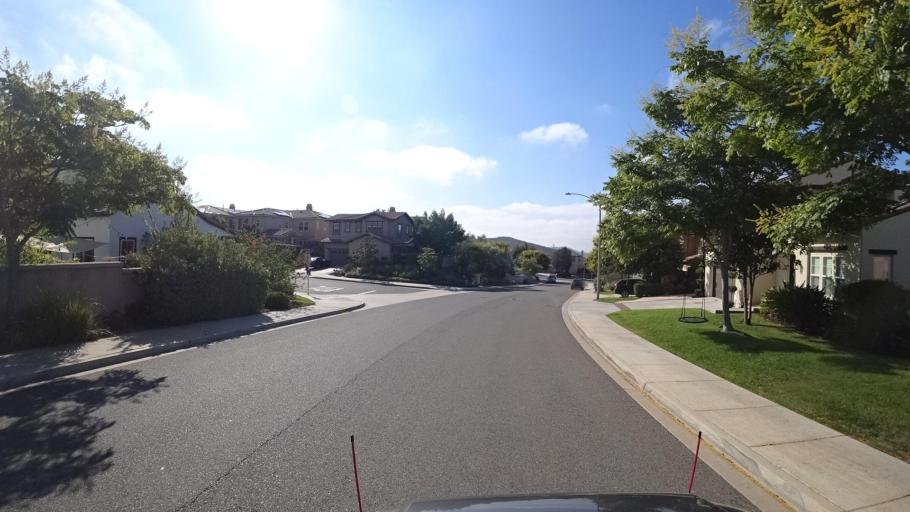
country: US
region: California
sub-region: San Diego County
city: Lake San Marcos
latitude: 33.1011
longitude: -117.1806
